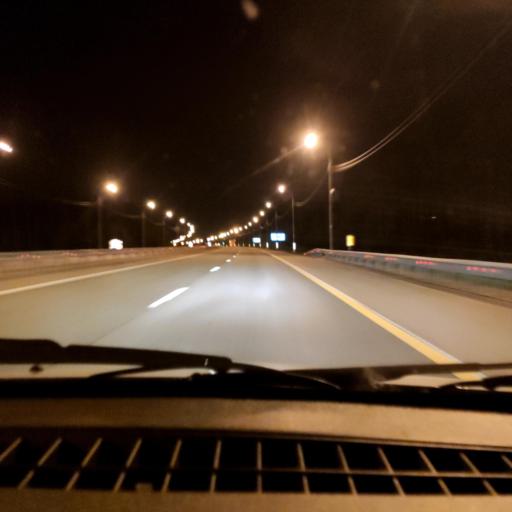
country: RU
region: Lipetsk
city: Khlevnoye
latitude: 52.2945
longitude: 39.0514
